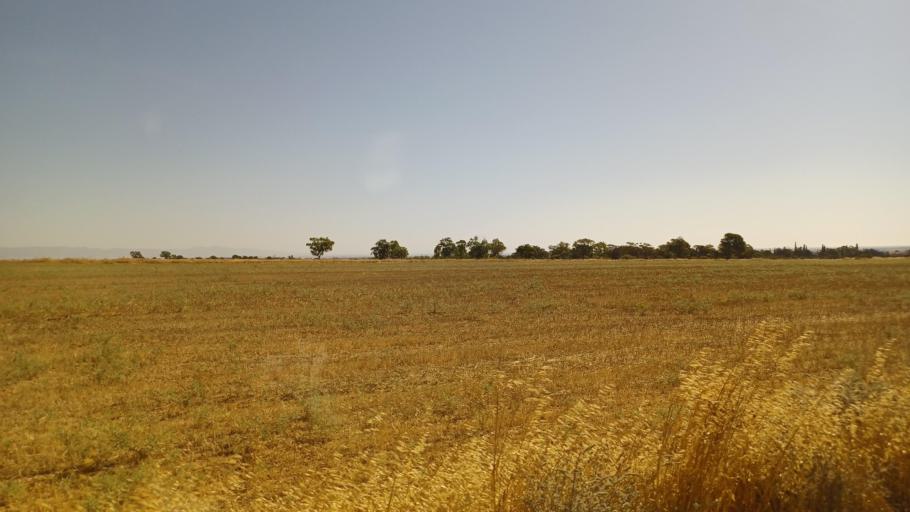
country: CY
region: Larnaka
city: Pergamos
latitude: 35.0407
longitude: 33.6873
